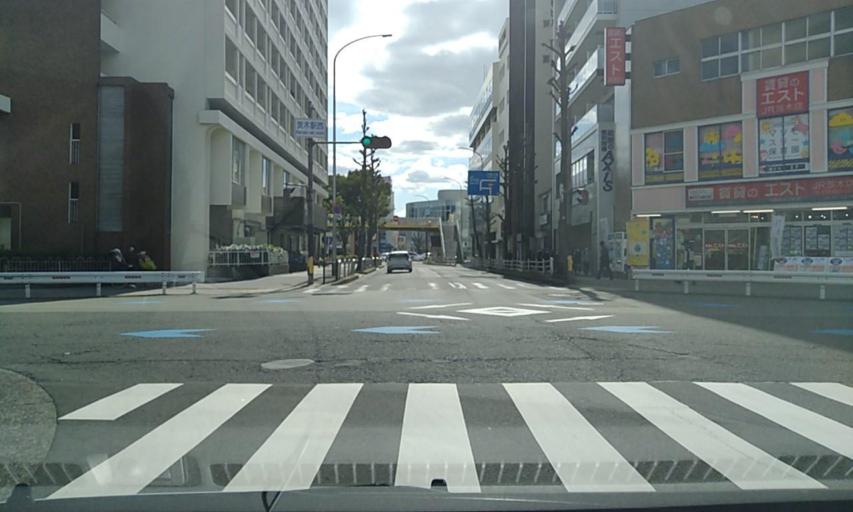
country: JP
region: Osaka
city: Ibaraki
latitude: 34.8171
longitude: 135.5614
